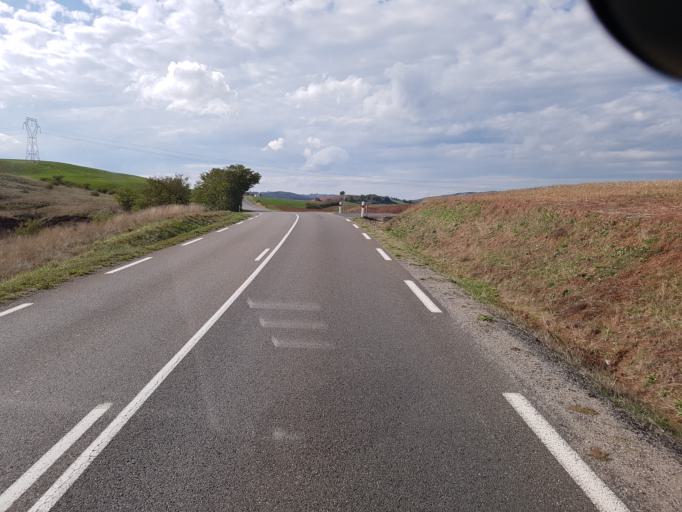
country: FR
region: Midi-Pyrenees
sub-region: Departement de l'Aveyron
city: Belmont-sur-Rance
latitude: 43.8773
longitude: 2.7881
